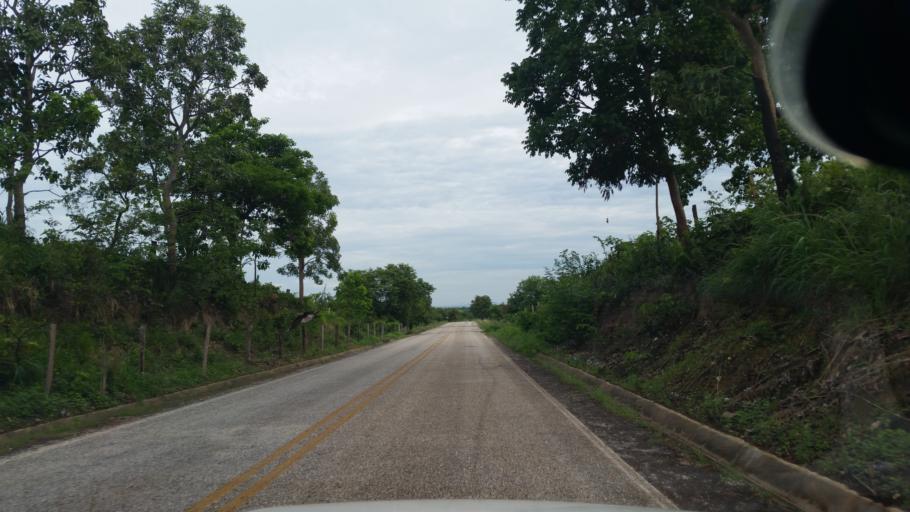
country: BR
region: Goias
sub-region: Uruacu
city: Uruacu
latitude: -14.0163
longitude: -49.1682
